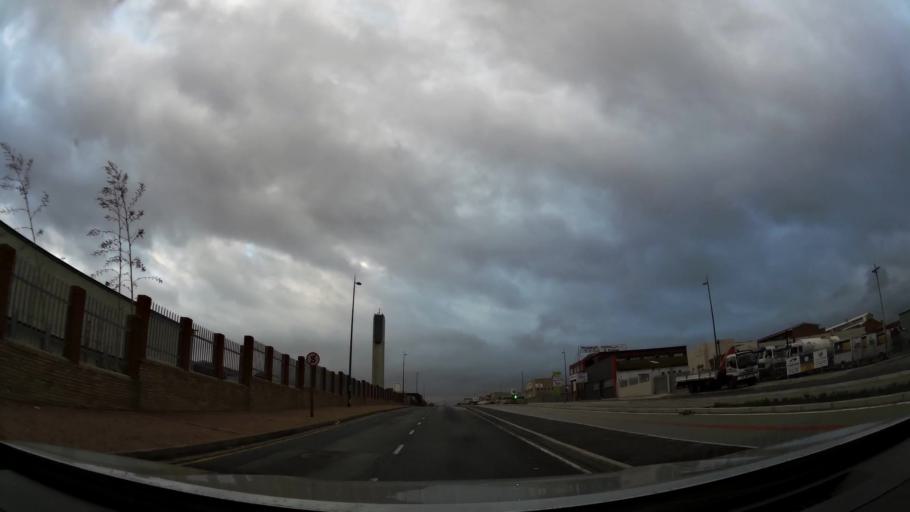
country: ZA
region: Eastern Cape
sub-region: Nelson Mandela Bay Metropolitan Municipality
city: Port Elizabeth
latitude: -33.9204
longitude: 25.5979
